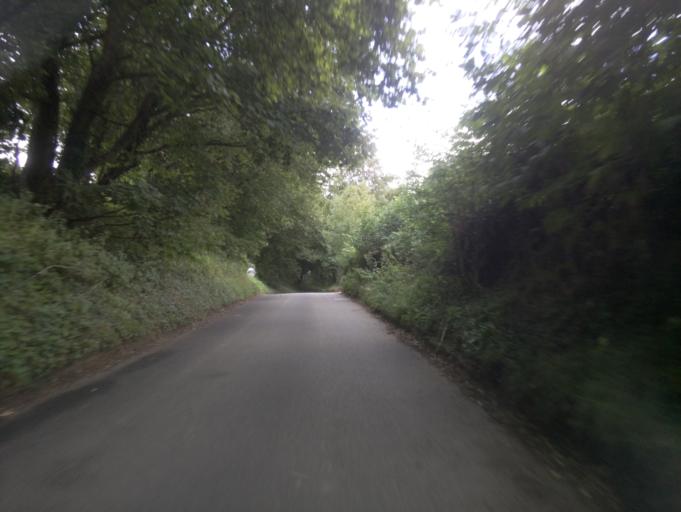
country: GB
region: England
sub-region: Wiltshire
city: Box
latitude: 51.4206
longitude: -2.2569
